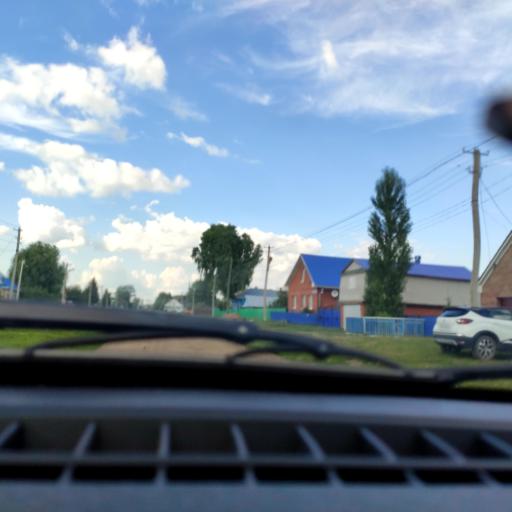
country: RU
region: Bashkortostan
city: Mikhaylovka
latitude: 54.9510
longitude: 55.7658
